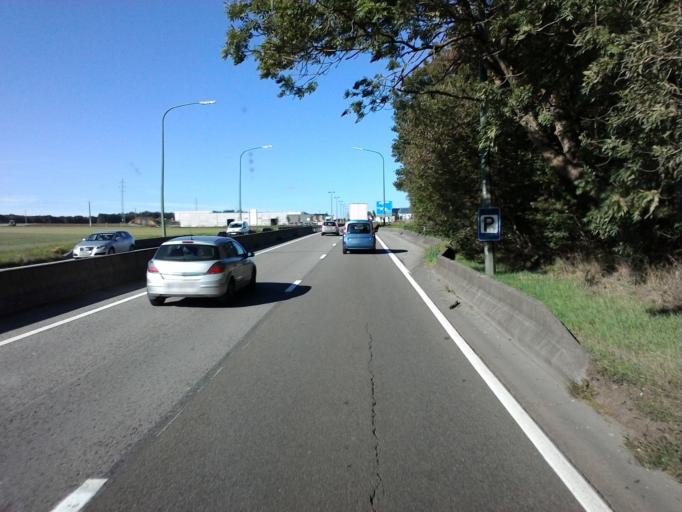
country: BE
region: Wallonia
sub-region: Province du Luxembourg
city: Messancy
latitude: 49.6324
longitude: 5.8132
